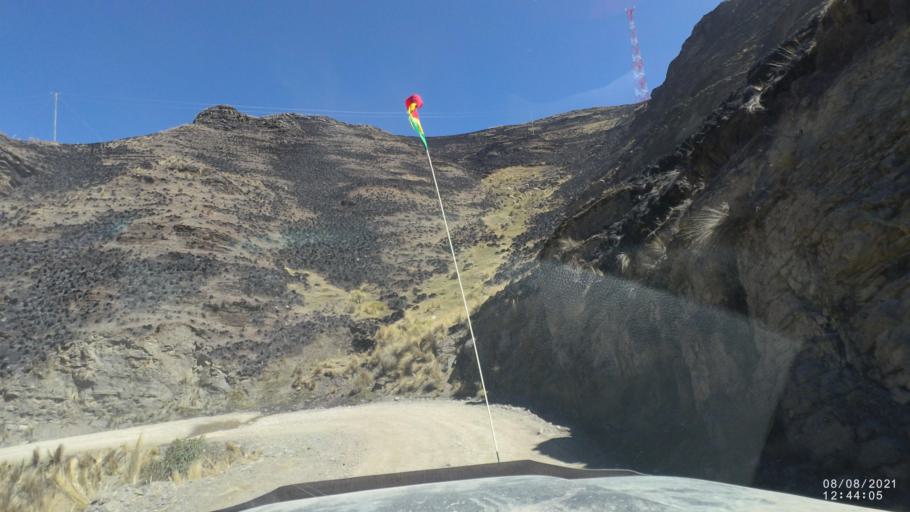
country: BO
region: Cochabamba
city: Colchani
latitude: -16.8447
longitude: -66.6119
